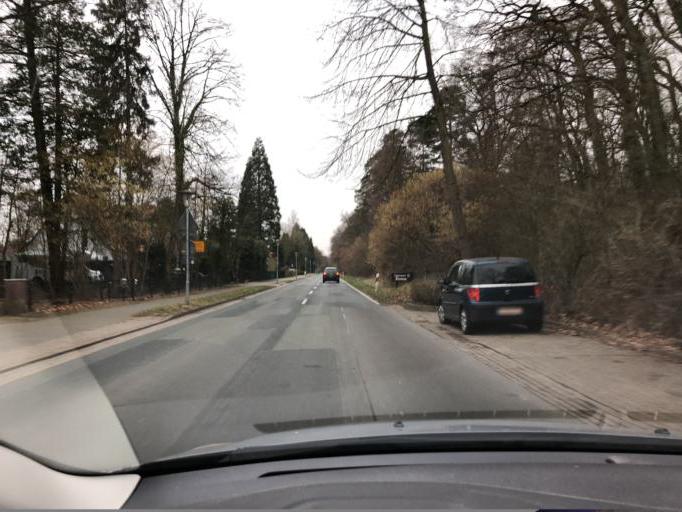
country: DE
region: Lower Saxony
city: Ganderkesee
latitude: 53.0823
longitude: 8.5743
